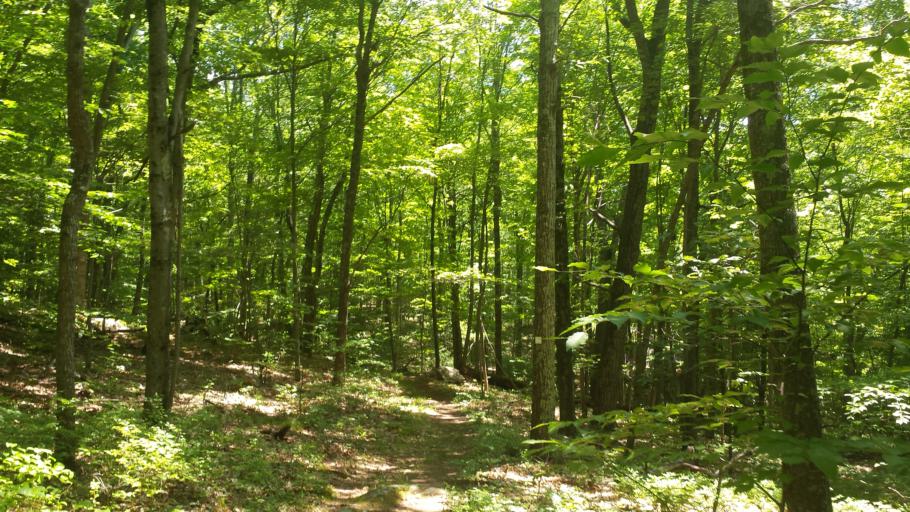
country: US
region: New York
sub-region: Westchester County
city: Pound Ridge
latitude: 41.2650
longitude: -73.5774
